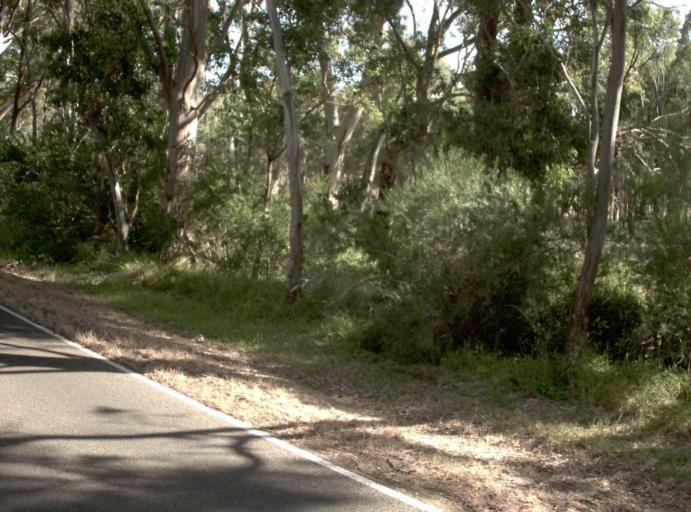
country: AU
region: Victoria
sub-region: East Gippsland
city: Lakes Entrance
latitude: -37.8062
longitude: 147.8407
